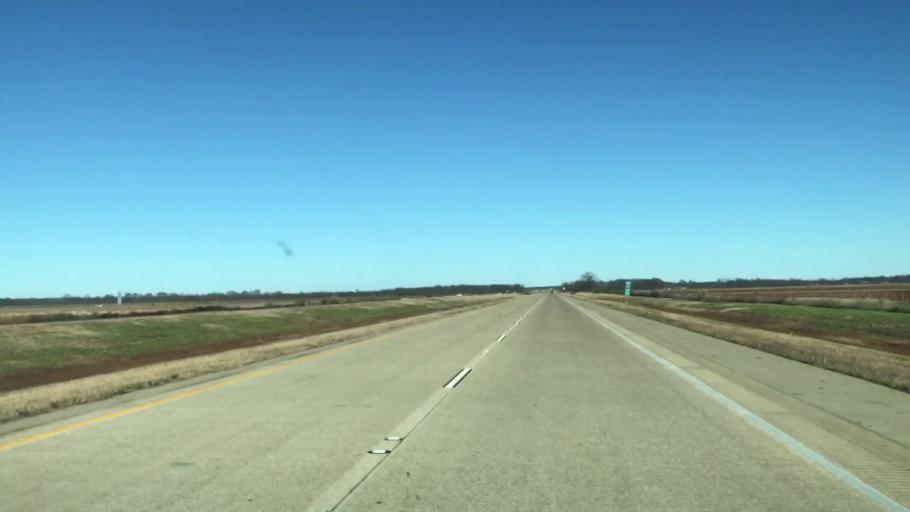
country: US
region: Louisiana
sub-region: Caddo Parish
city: Oil City
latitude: 32.7249
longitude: -93.8708
